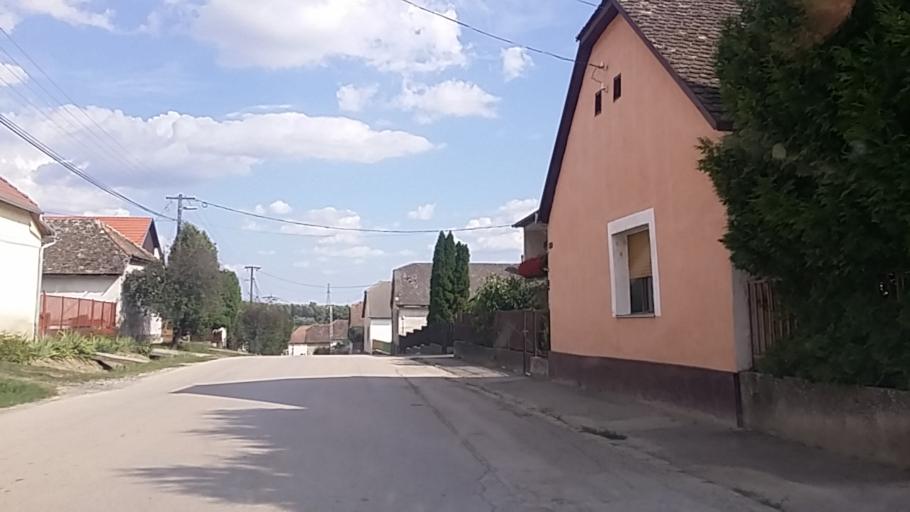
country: HU
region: Tolna
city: Gyonk
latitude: 46.5503
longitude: 18.4839
